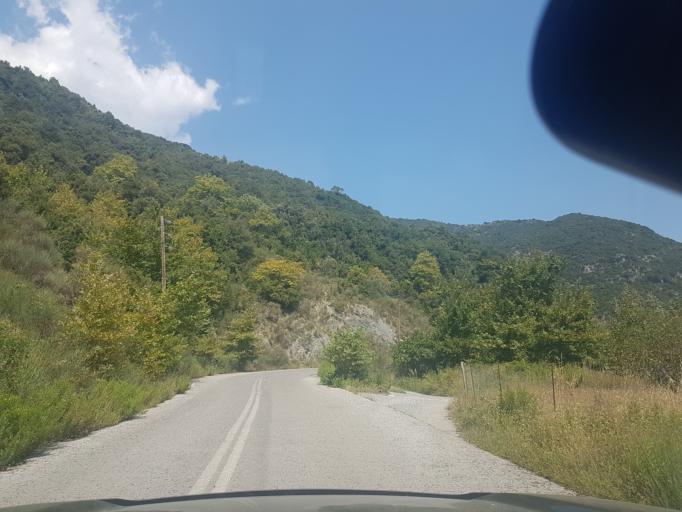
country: GR
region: Central Greece
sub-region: Nomos Evvoias
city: Yimnon
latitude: 38.6341
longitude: 23.8904
